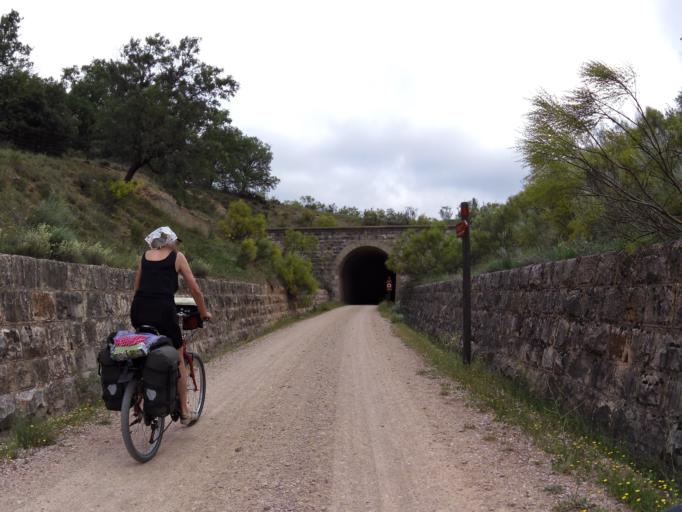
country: ES
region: Castille-La Mancha
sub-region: Provincia de Albacete
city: Robledo
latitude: 38.7266
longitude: -2.4775
